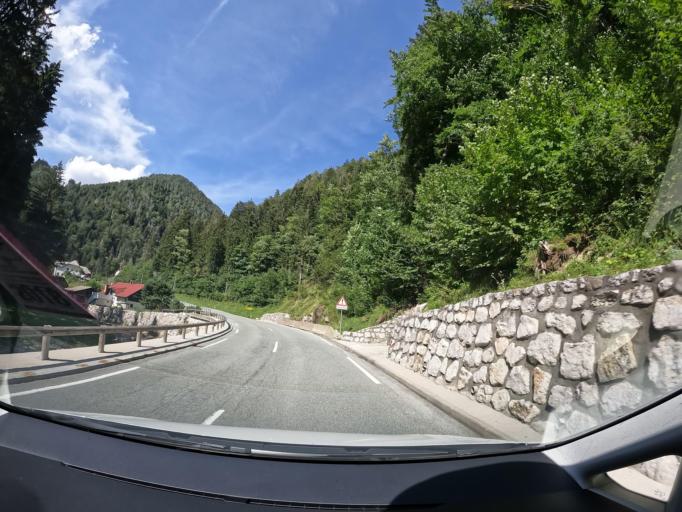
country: SI
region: Trzic
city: Trzic
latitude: 46.4064
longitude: 14.3154
